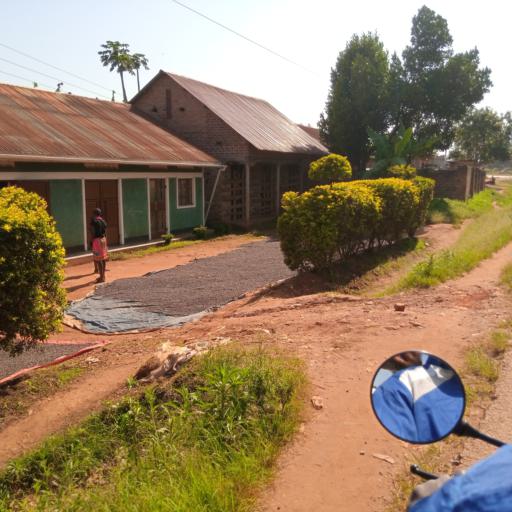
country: UG
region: Central Region
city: Masaka
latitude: -0.3774
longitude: 31.7125
